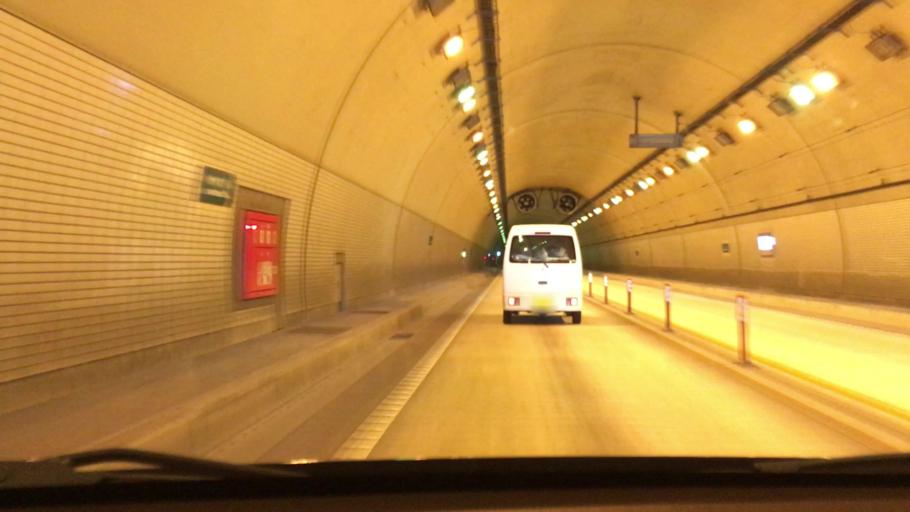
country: JP
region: Nagasaki
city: Sasebo
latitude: 33.0886
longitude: 129.7783
